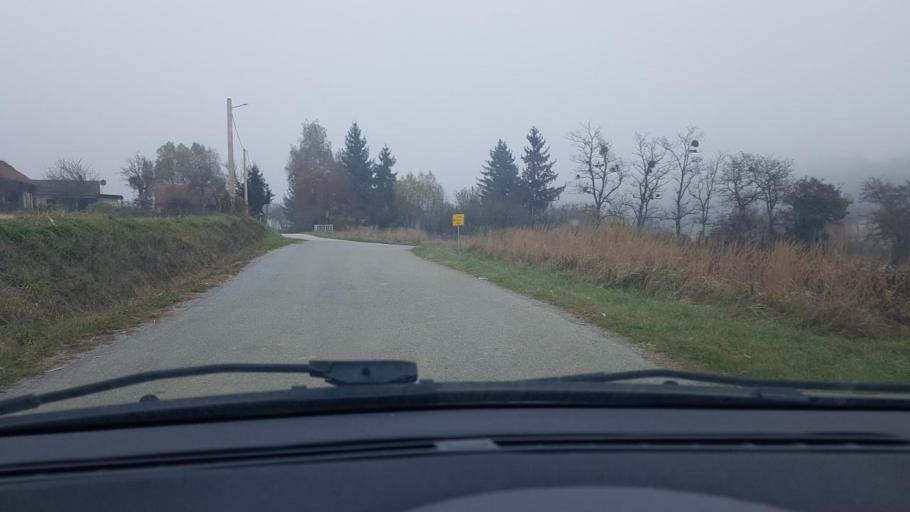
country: HR
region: Krapinsko-Zagorska
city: Mihovljan
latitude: 46.1490
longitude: 15.9839
